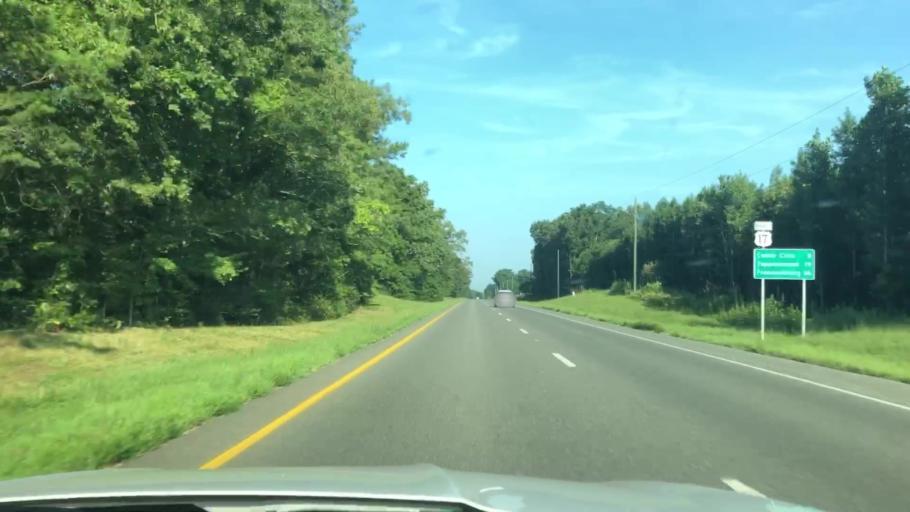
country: US
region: Virginia
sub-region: Middlesex County
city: Saluda
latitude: 37.7177
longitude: -76.7010
